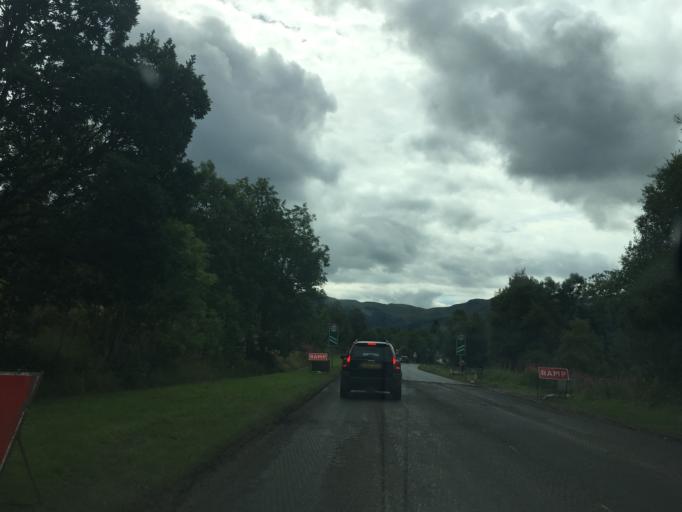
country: GB
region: Scotland
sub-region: Stirling
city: Callander
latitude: 56.3305
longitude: -4.3248
